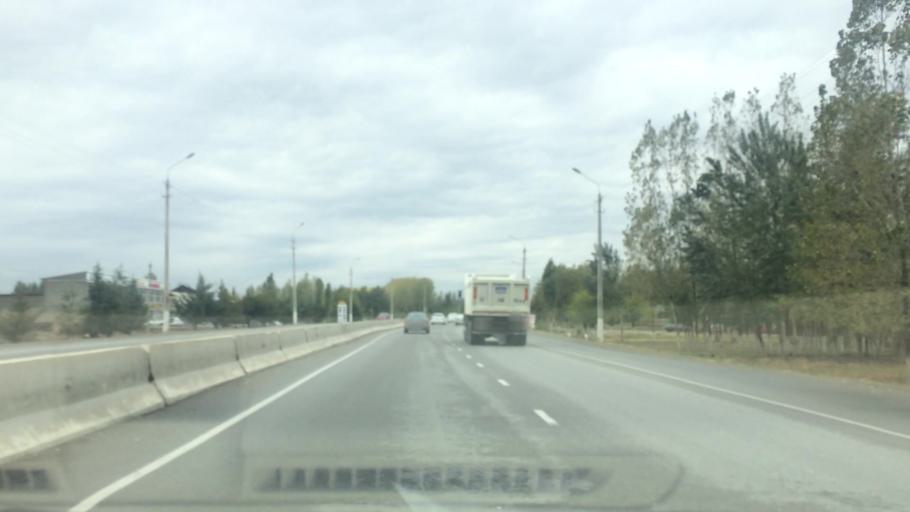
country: UZ
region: Jizzax
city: Jizzax
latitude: 39.9918
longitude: 67.5840
